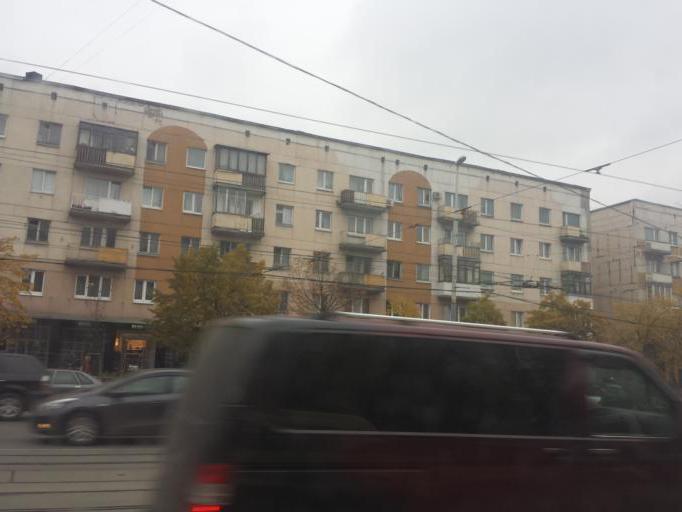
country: RU
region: Kaliningrad
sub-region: Gorod Kaliningrad
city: Kaliningrad
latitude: 54.7037
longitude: 20.5054
